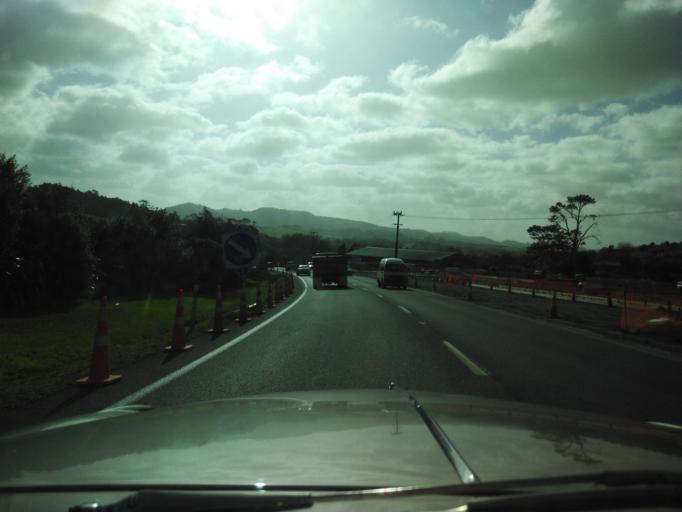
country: NZ
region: Auckland
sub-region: Auckland
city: Warkworth
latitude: -36.4093
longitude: 174.6590
